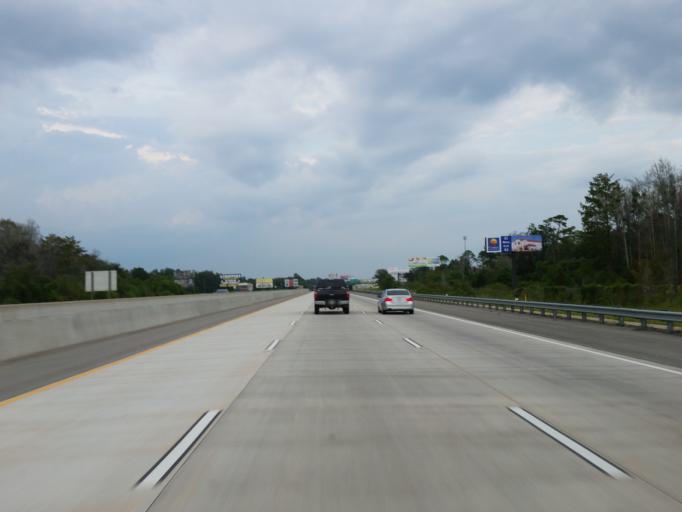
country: US
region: Georgia
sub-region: Cook County
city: Sparks
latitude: 31.1566
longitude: -83.4465
